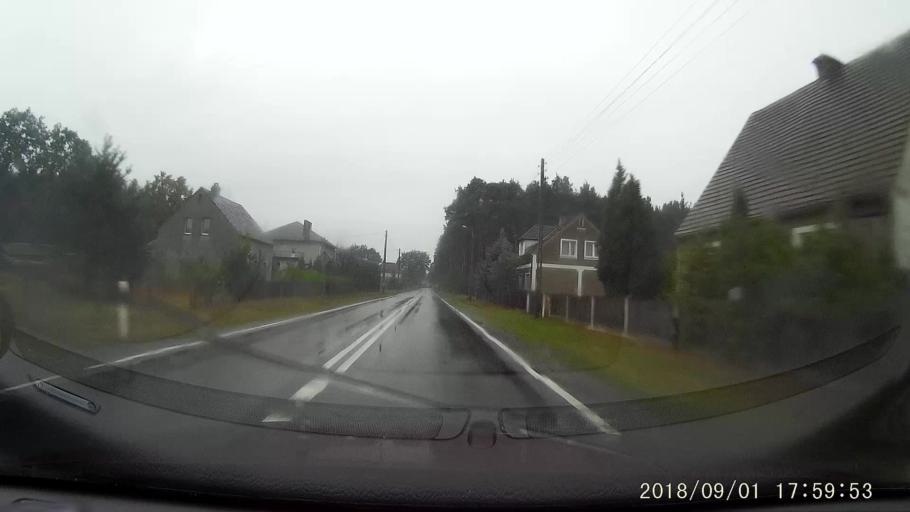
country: PL
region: Lubusz
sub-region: Powiat zaganski
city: Gozdnica
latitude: 51.4063
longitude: 15.1832
